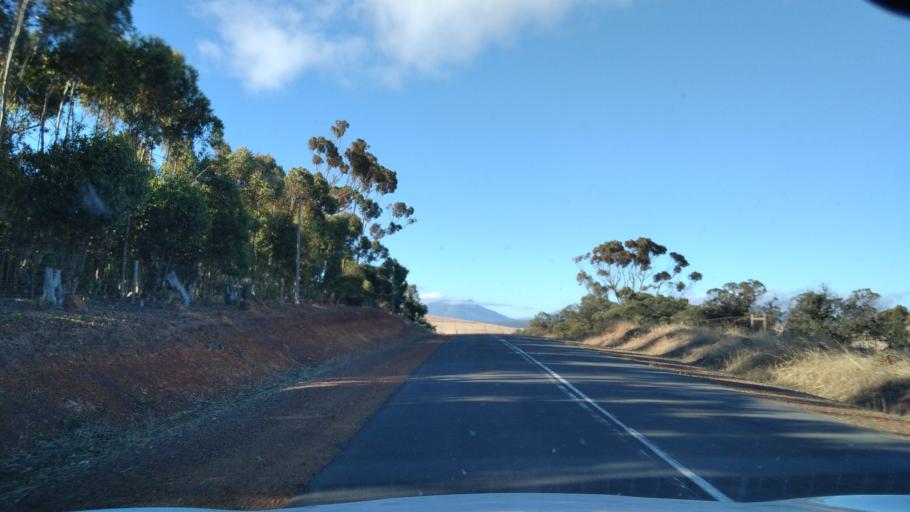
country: ZA
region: Western Cape
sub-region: Overberg District Municipality
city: Caledon
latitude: -34.1996
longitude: 19.2695
